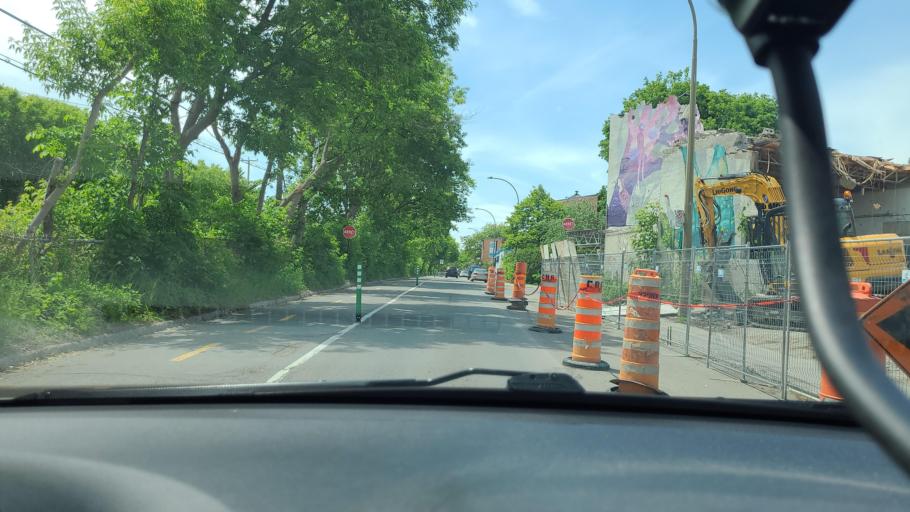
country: CA
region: Quebec
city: Saint-Raymond
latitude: 45.4686
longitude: -73.6133
